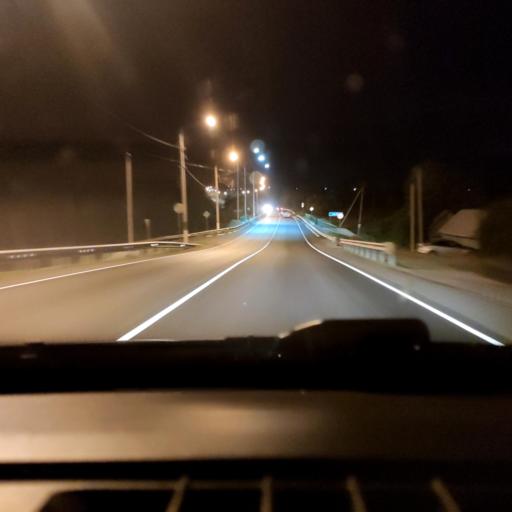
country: RU
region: Voronezj
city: Panino
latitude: 51.4877
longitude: 40.2114
